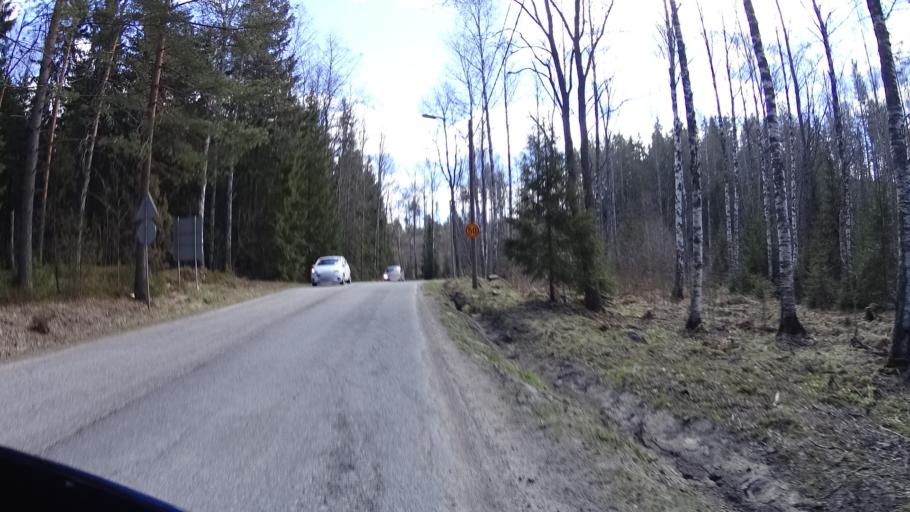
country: FI
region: Uusimaa
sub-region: Helsinki
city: Espoo
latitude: 60.2723
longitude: 24.5186
